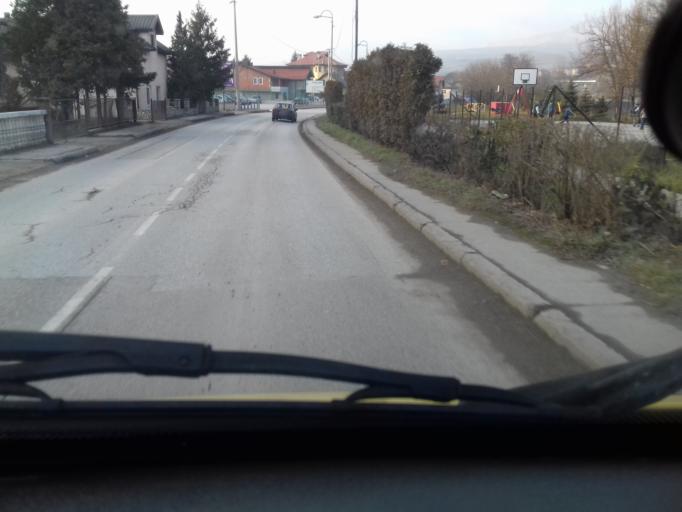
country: BA
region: Federation of Bosnia and Herzegovina
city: Kakanj
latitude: 44.1186
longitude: 18.1153
